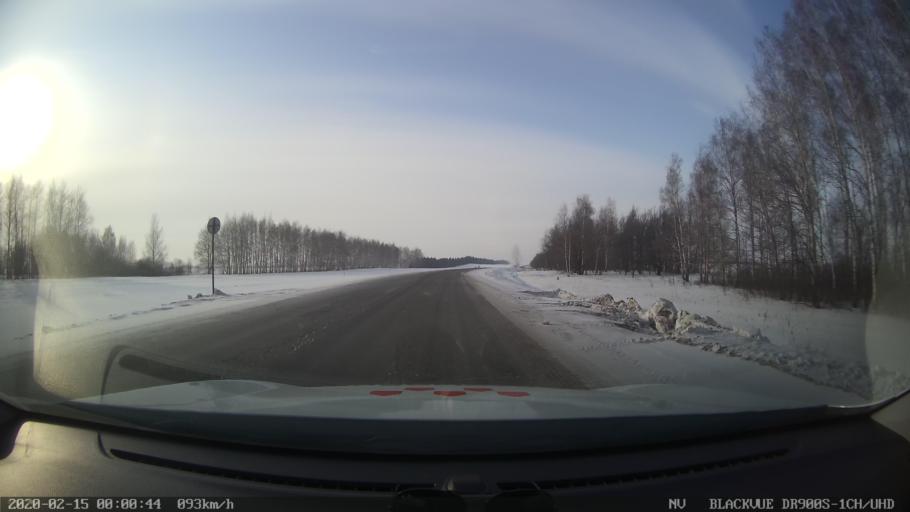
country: RU
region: Tatarstan
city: Kuybyshevskiy Zaton
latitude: 55.3440
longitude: 49.0317
